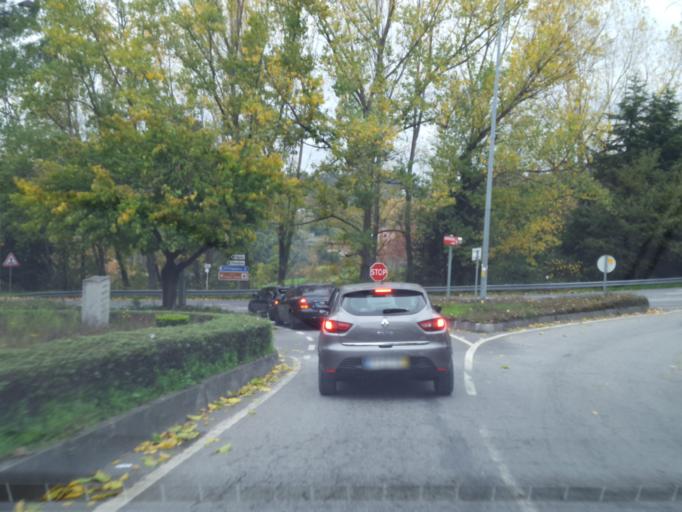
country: PT
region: Porto
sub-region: Marco de Canaveses
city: Marco de Canavezes
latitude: 41.1935
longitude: -8.1544
